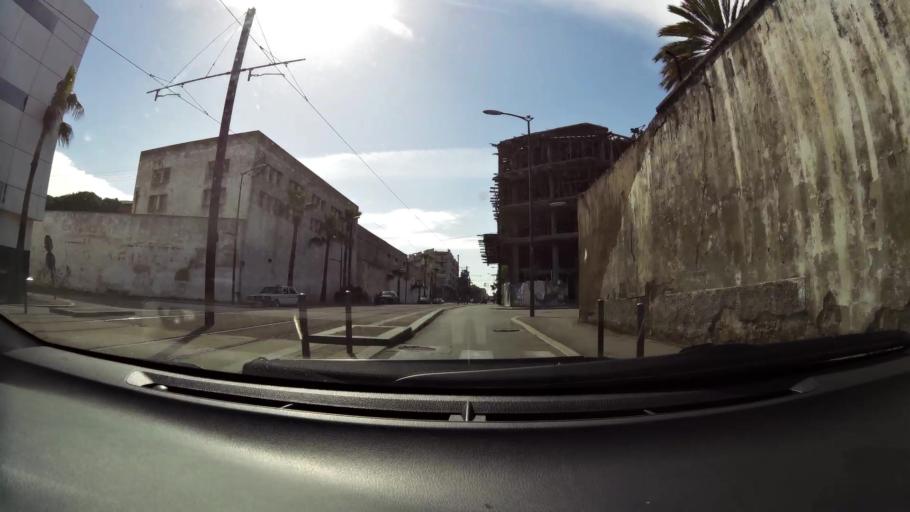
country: MA
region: Grand Casablanca
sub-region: Casablanca
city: Casablanca
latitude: 33.5922
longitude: -7.5810
